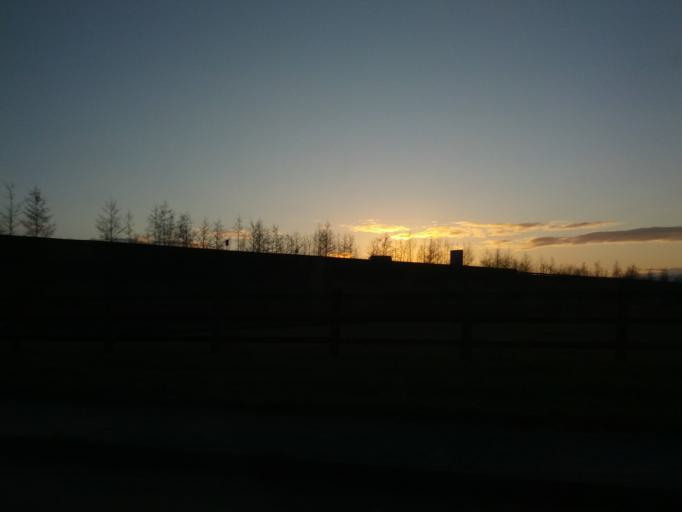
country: IE
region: Connaught
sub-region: County Galway
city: Athenry
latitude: 53.2823
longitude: -8.7432
